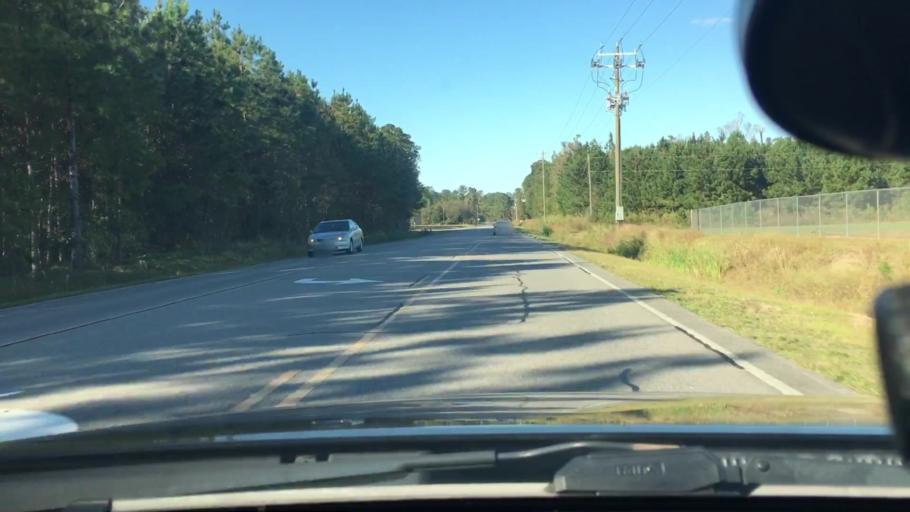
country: US
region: North Carolina
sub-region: Craven County
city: Vanceboro
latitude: 35.2341
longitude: -77.1359
